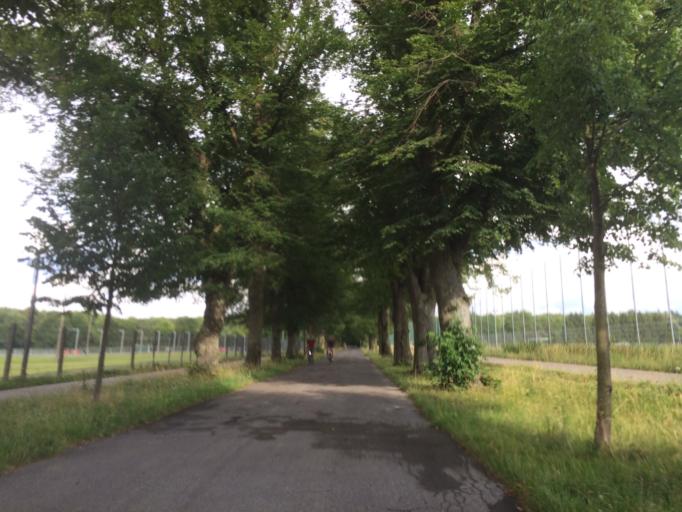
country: DE
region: Bavaria
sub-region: Swabia
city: Augsburg
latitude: 48.3392
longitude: 10.9111
